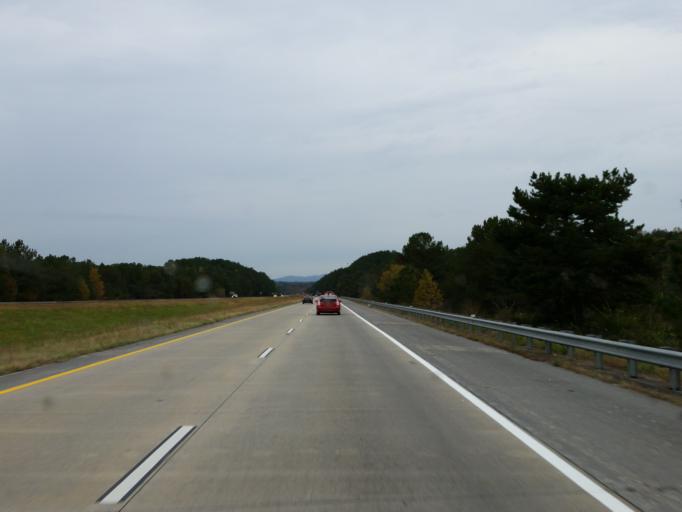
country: US
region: Georgia
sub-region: Pickens County
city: Nelson
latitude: 34.3653
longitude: -84.3909
